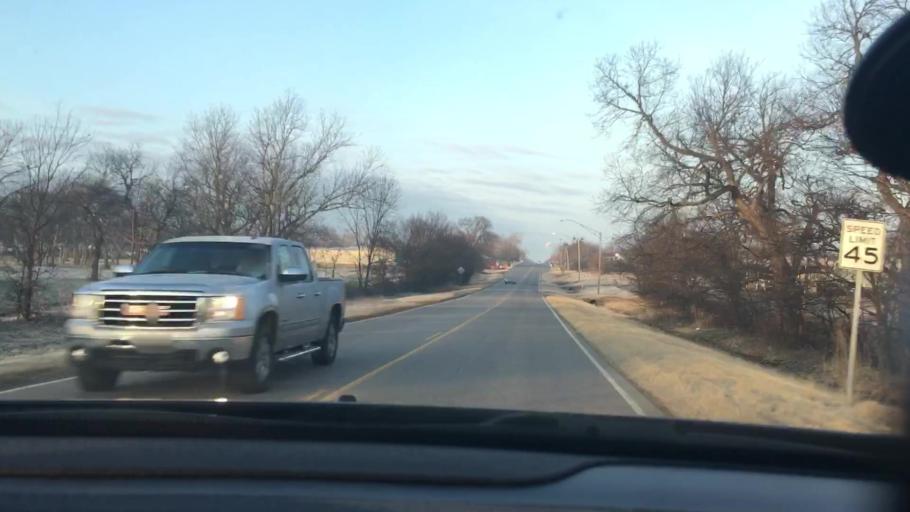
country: US
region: Oklahoma
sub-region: Garvin County
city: Stratford
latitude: 34.7974
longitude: -96.9464
